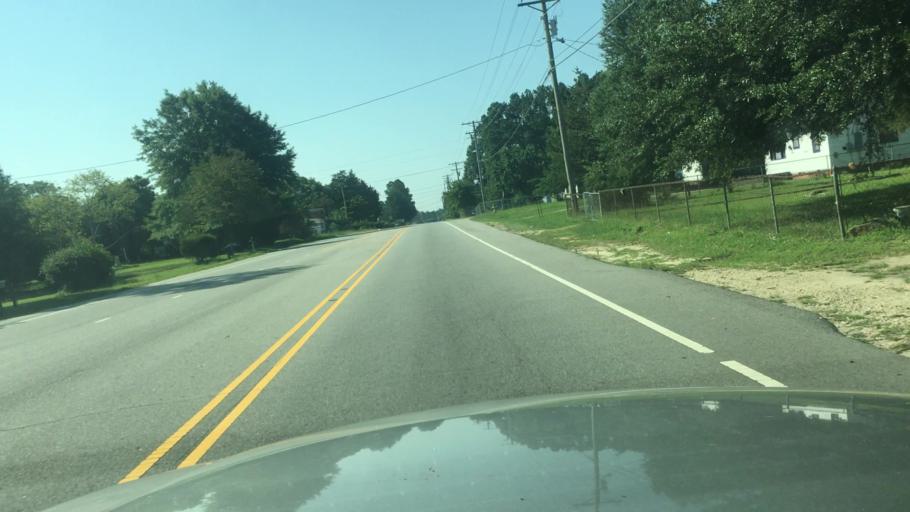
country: US
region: North Carolina
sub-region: Cumberland County
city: Spring Lake
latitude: 35.1494
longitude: -78.9117
